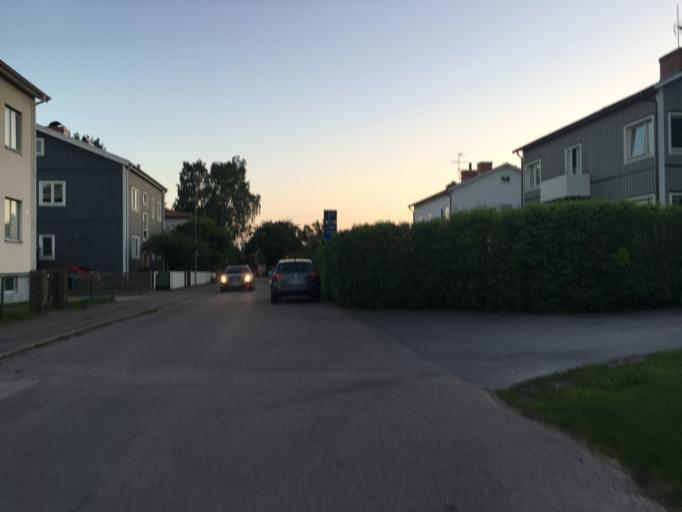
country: SE
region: Kalmar
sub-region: Kalmar Kommun
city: Kalmar
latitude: 56.6578
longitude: 16.3358
